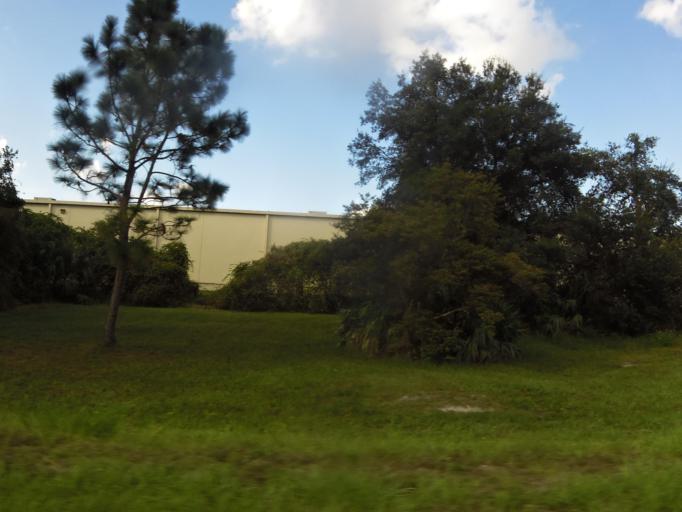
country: US
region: Florida
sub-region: Duval County
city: Jacksonville Beach
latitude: 30.2760
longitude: -81.5058
